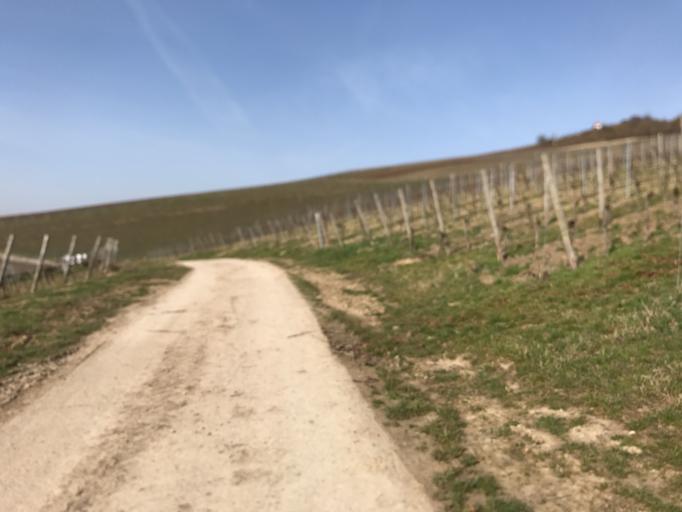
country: DE
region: Rheinland-Pfalz
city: Stadecken-Elsheim
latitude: 49.9167
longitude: 8.1400
